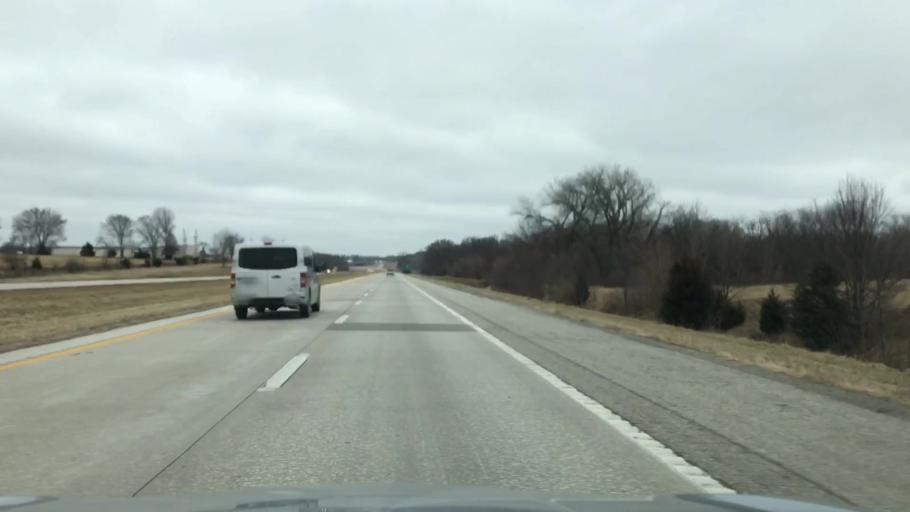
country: US
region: Missouri
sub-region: Linn County
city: Brookfield
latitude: 39.7774
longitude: -93.0958
